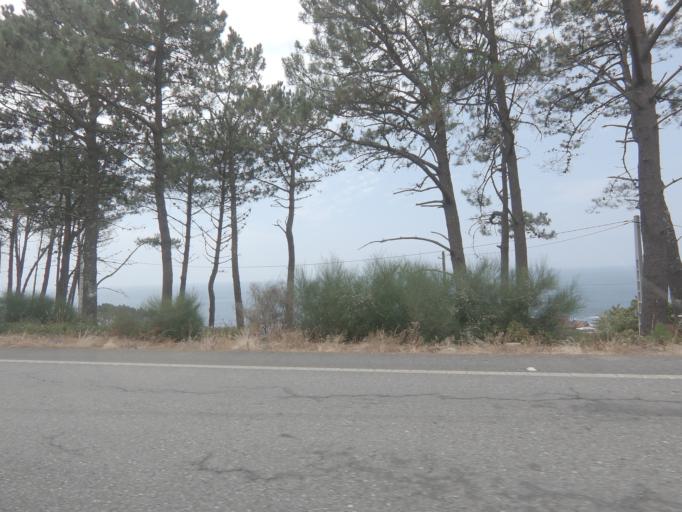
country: ES
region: Galicia
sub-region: Provincia de Pontevedra
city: Oia
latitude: 41.9617
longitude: -8.8836
